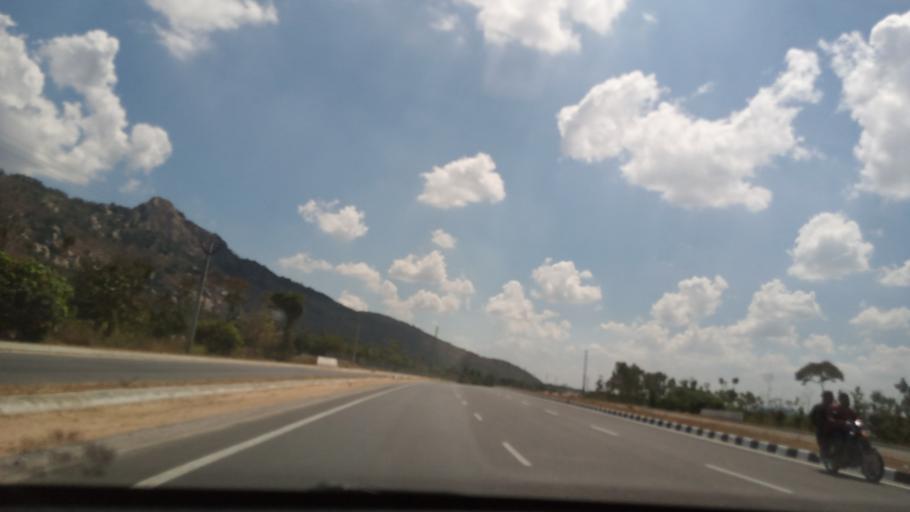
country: IN
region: Andhra Pradesh
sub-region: Chittoor
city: Chittoor
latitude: 13.3307
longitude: 79.0753
